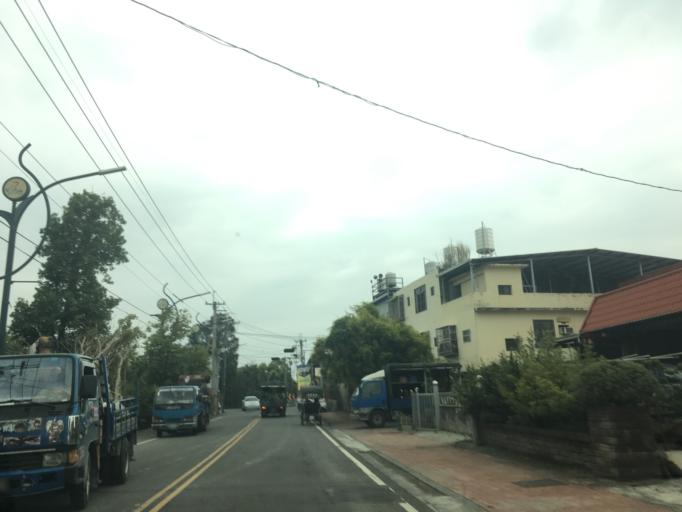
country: TW
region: Taiwan
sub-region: Nantou
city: Nantou
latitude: 23.9022
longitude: 120.5329
